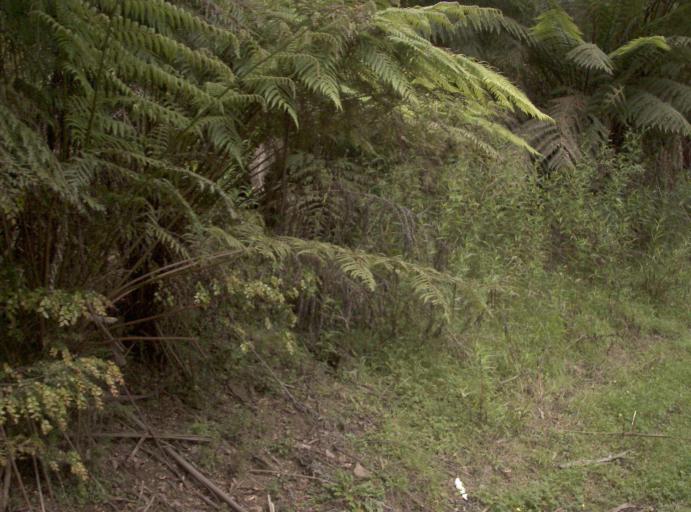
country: AU
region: Victoria
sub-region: Latrobe
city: Traralgon
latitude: -38.4492
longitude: 146.5382
